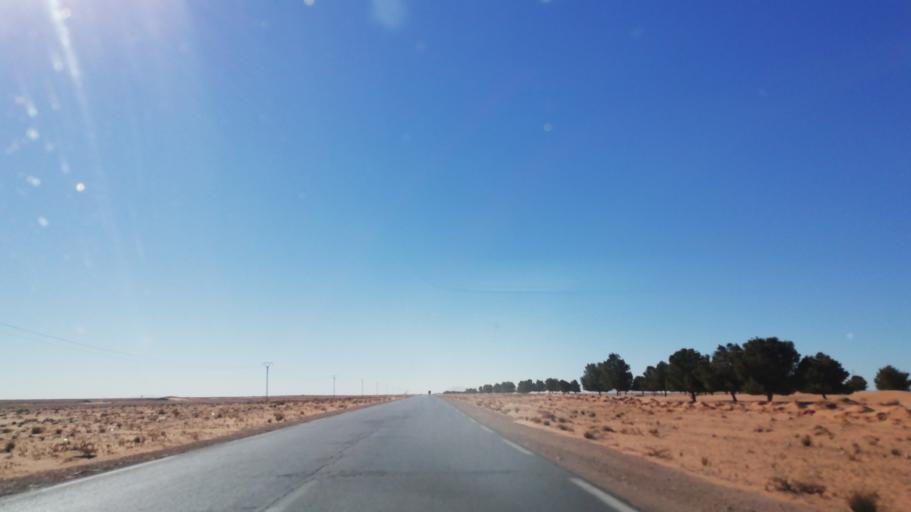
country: DZ
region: Wilaya de Naama
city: Naama
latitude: 33.9731
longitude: 0.0227
